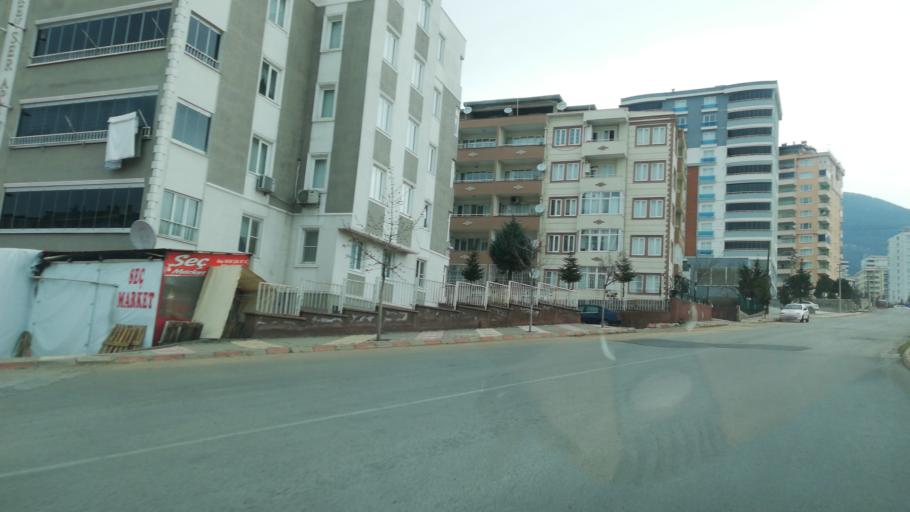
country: TR
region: Kahramanmaras
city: Kahramanmaras
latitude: 37.5932
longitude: 36.8905
